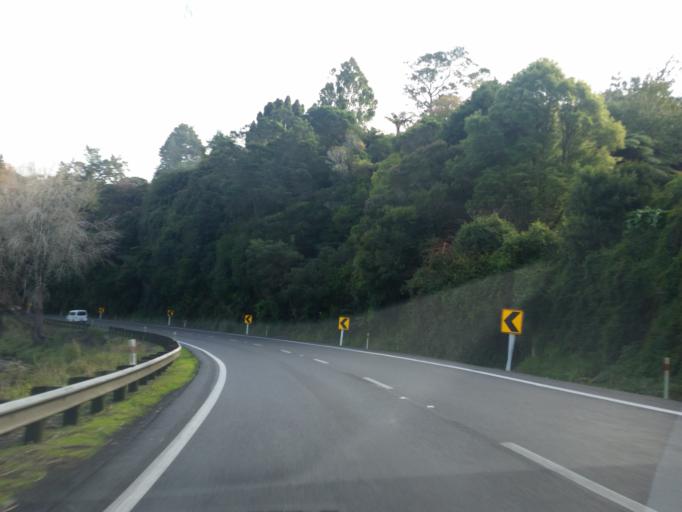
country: NZ
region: Waikato
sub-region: Hauraki District
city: Waihi
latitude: -37.4113
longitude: 175.7776
